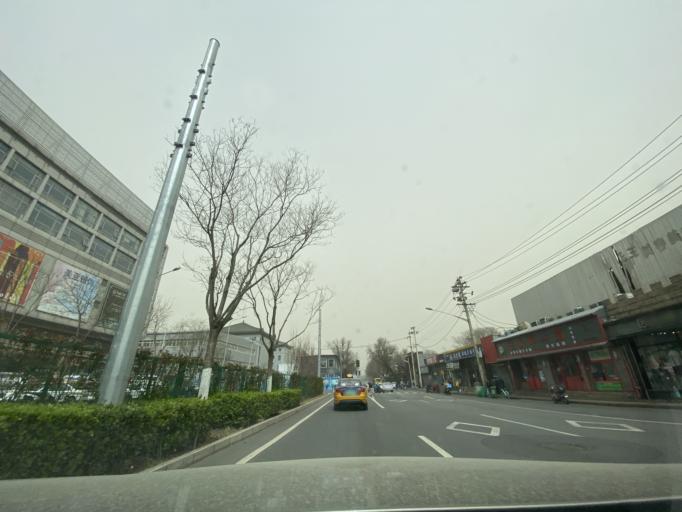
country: CN
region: Beijing
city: Jinrongjie
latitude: 39.9423
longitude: 116.3661
